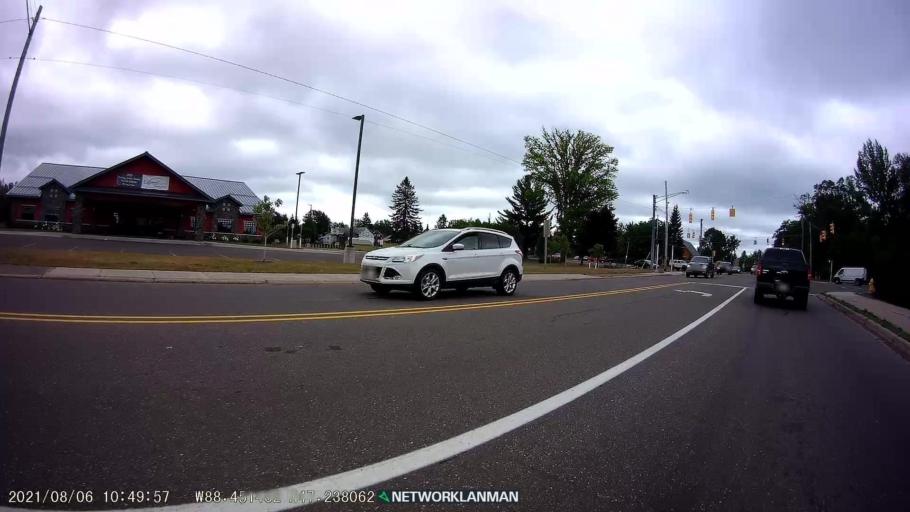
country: US
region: Michigan
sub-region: Houghton County
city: Laurium
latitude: 47.2379
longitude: -88.4516
